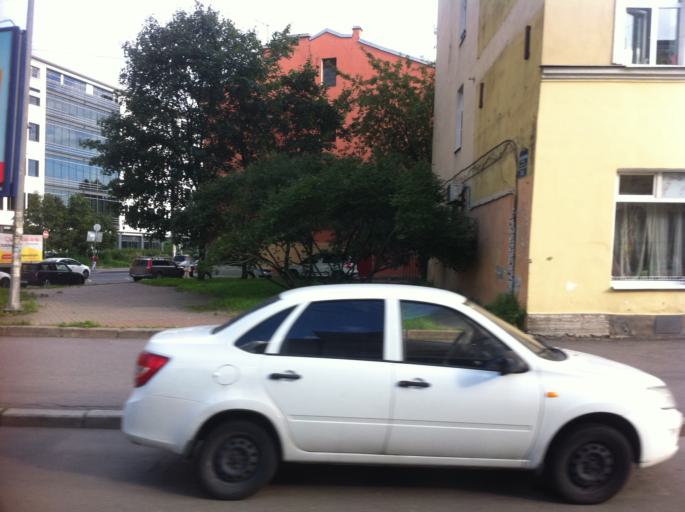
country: RU
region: St.-Petersburg
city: Admiralteisky
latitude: 59.9058
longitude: 30.2760
